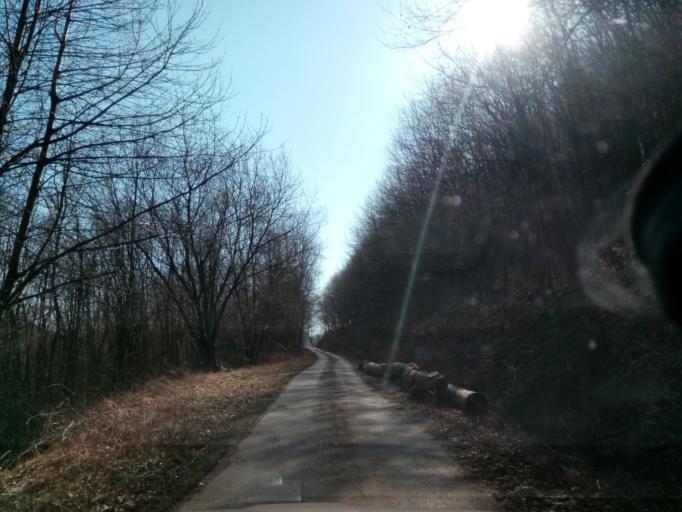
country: SK
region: Kosicky
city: Roznava
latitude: 48.5530
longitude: 20.5641
